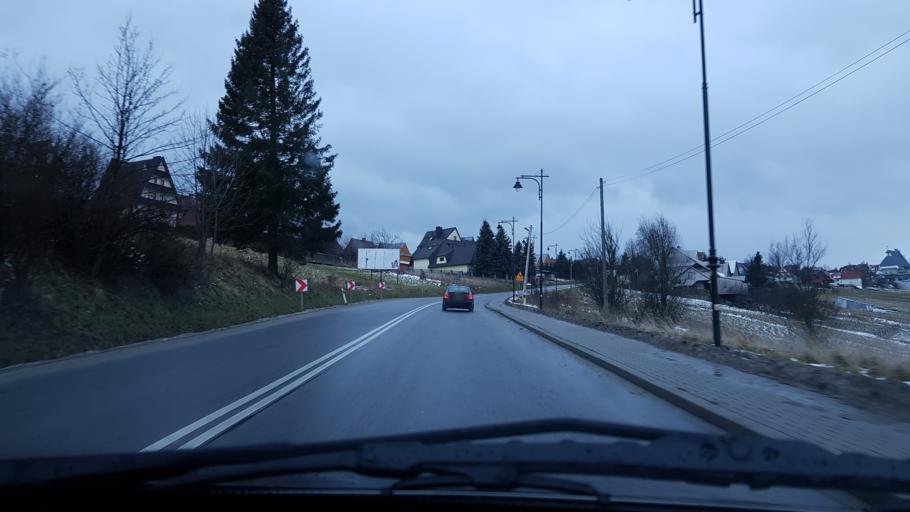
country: PL
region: Lesser Poland Voivodeship
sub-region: Powiat tatrzanski
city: Bukowina Tatrzanska
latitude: 49.3482
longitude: 20.1166
